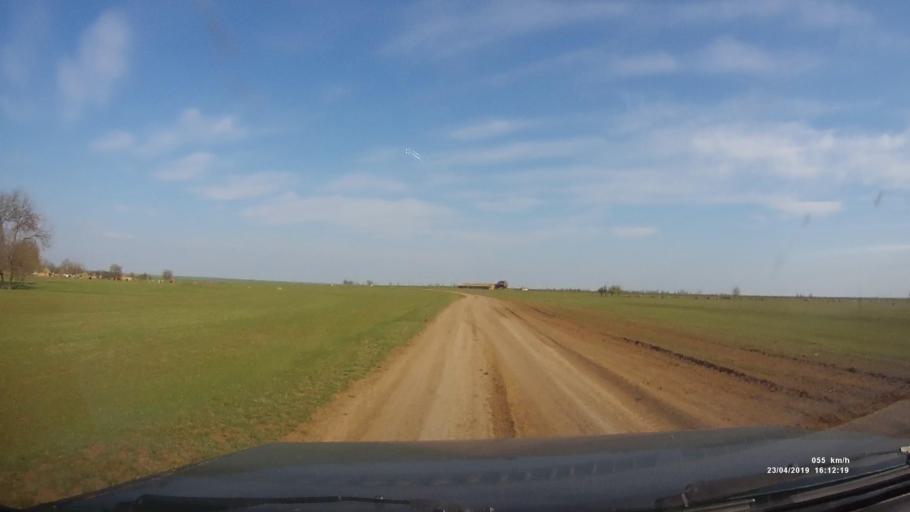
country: RU
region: Kalmykiya
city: Priyutnoye
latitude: 46.4670
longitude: 43.1252
